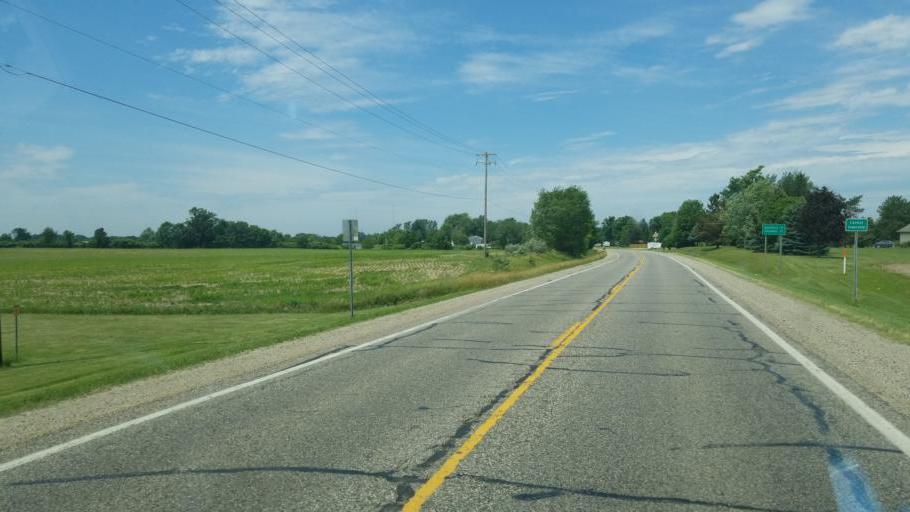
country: US
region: Michigan
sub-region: Eaton County
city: Charlotte
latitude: 42.5664
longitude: -84.8562
